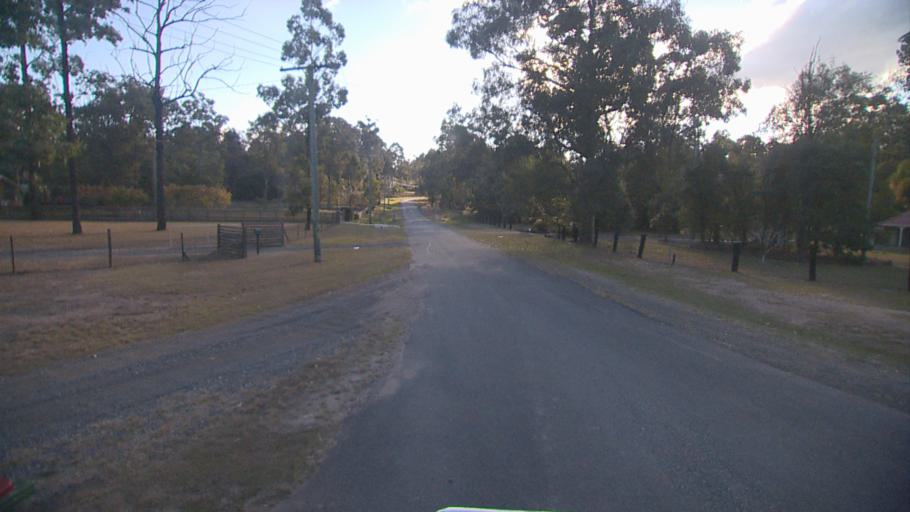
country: AU
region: Queensland
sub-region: Ipswich
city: Springfield Lakes
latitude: -27.7003
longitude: 152.9568
